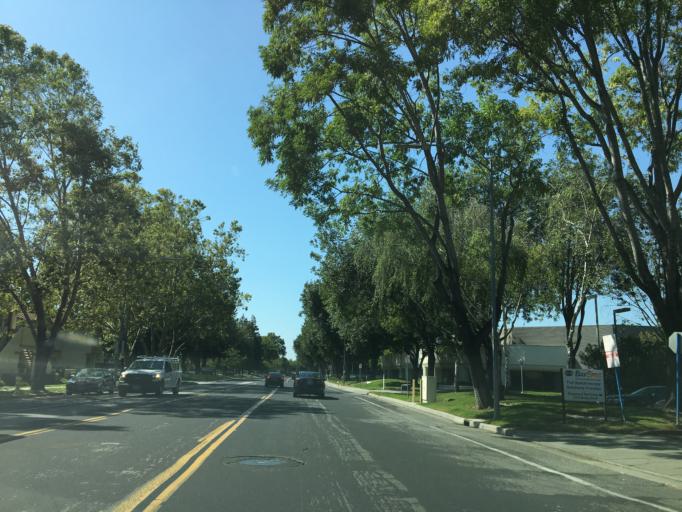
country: US
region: California
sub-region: Santa Clara County
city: Milpitas
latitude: 37.3892
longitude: -121.8943
